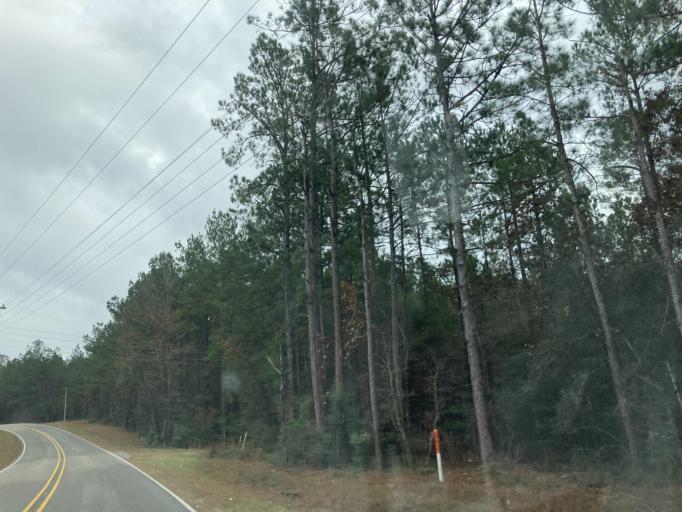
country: US
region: Mississippi
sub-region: Lamar County
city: Lumberton
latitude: 31.0653
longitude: -89.6140
